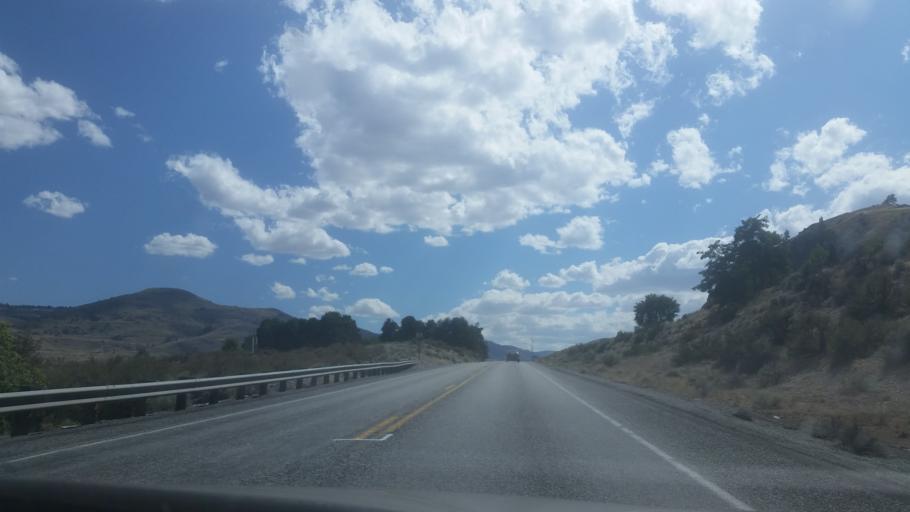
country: US
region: Washington
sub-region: Okanogan County
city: Brewster
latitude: 47.9532
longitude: -119.8770
